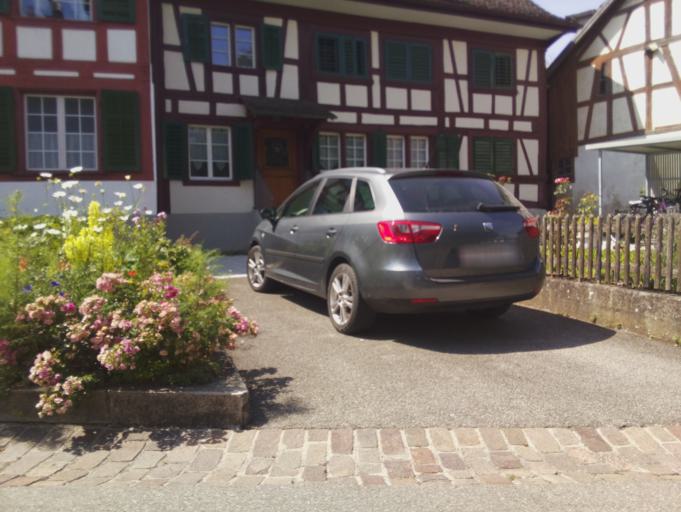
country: CH
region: Zurich
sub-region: Bezirk Andelfingen
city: Grossandelfingen
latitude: 47.5957
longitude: 8.6802
